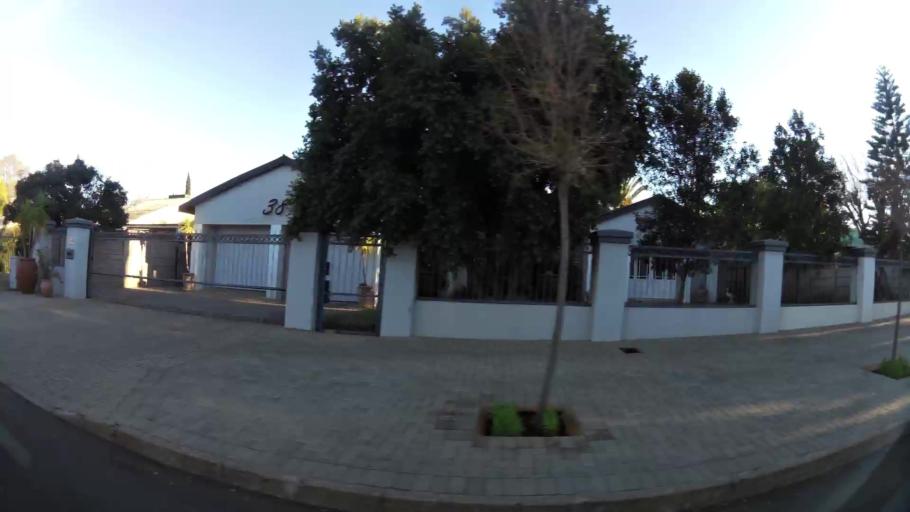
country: ZA
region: Northern Cape
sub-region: Frances Baard District Municipality
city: Kimberley
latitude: -28.7601
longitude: 24.7445
